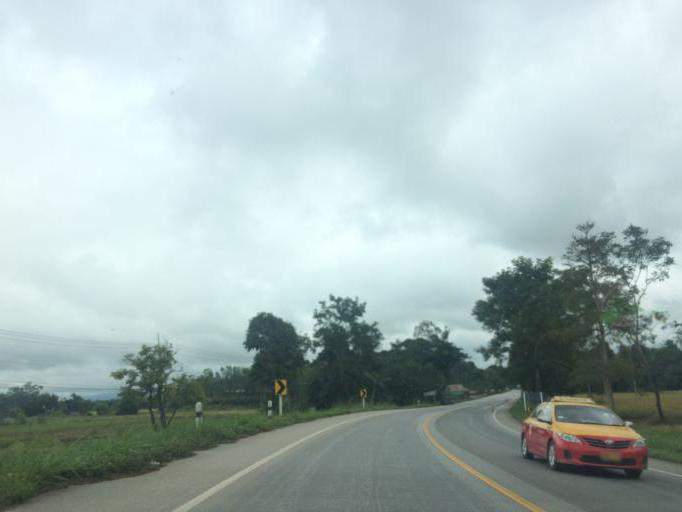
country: TH
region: Chiang Rai
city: Mae Lao
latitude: 19.7478
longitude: 99.6802
